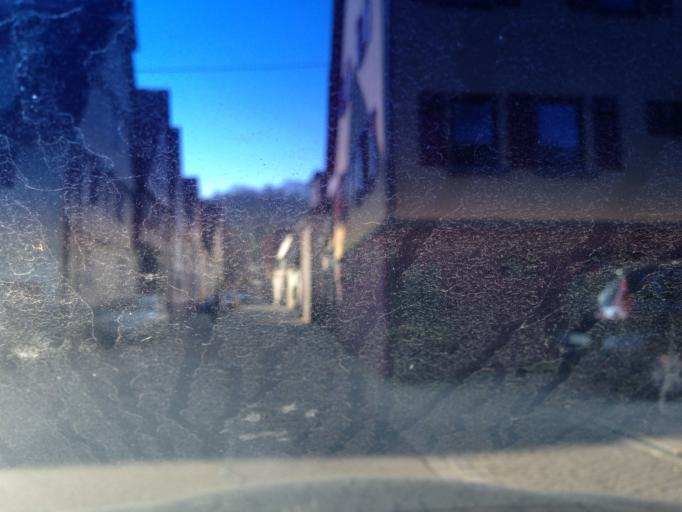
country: DE
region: Baden-Wuerttemberg
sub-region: Karlsruhe Region
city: Illingen
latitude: 48.9408
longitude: 8.8936
